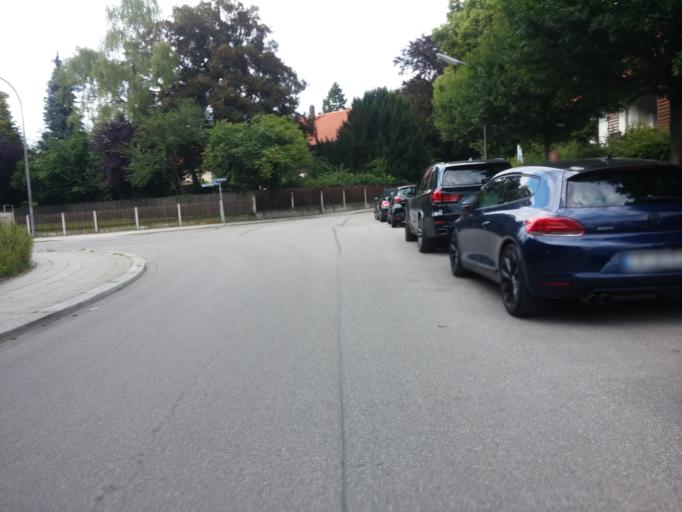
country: DE
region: Bavaria
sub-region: Upper Bavaria
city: Bogenhausen
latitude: 48.1582
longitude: 11.6436
